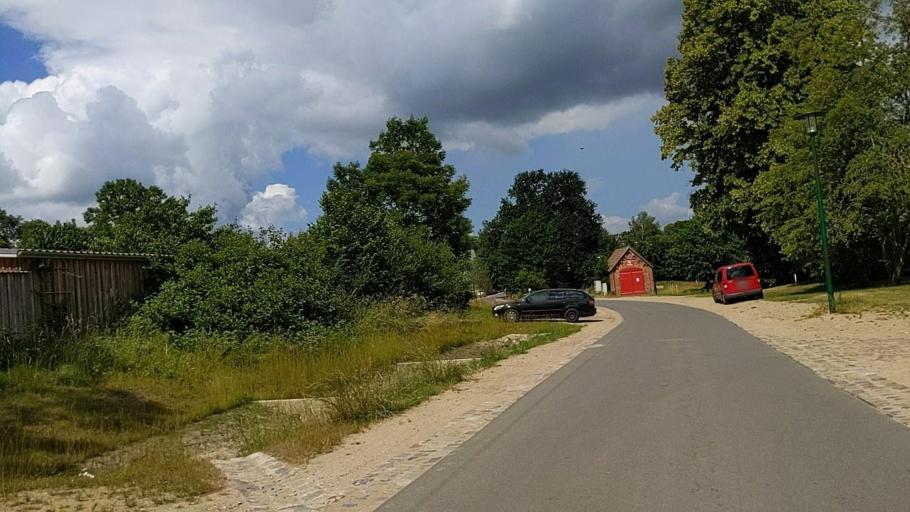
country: DE
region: Mecklenburg-Vorpommern
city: Selmsdorf
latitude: 53.8532
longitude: 10.8040
